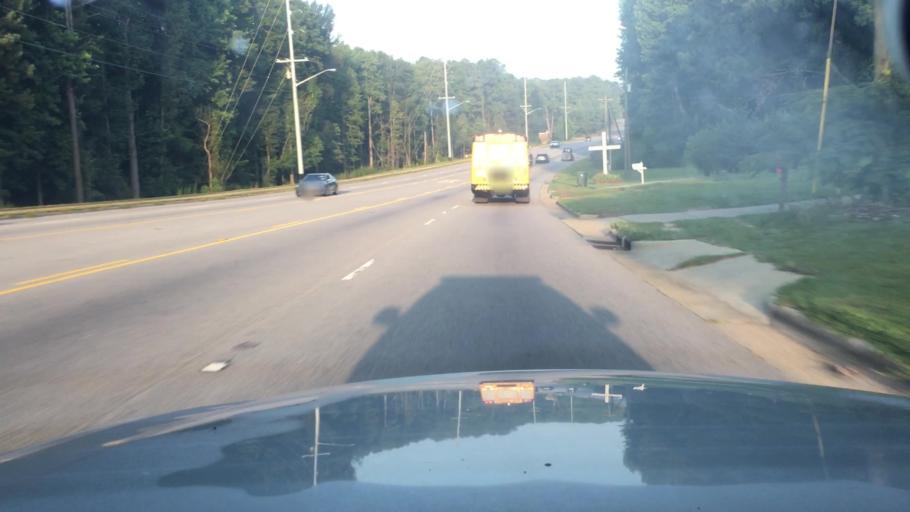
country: US
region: North Carolina
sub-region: Cumberland County
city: Fayetteville
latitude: 35.1010
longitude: -78.9039
